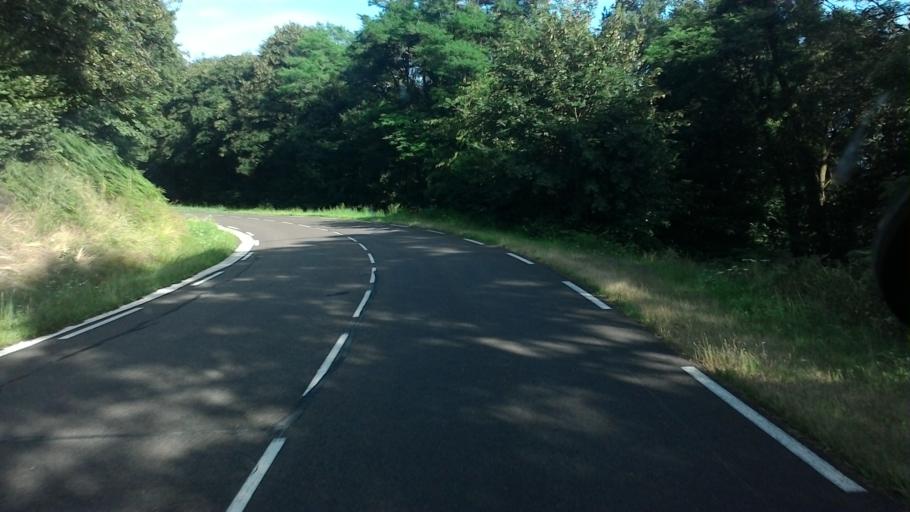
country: FR
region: Lorraine
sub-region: Departement des Vosges
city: Rupt-sur-Moselle
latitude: 47.8962
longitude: 6.6333
